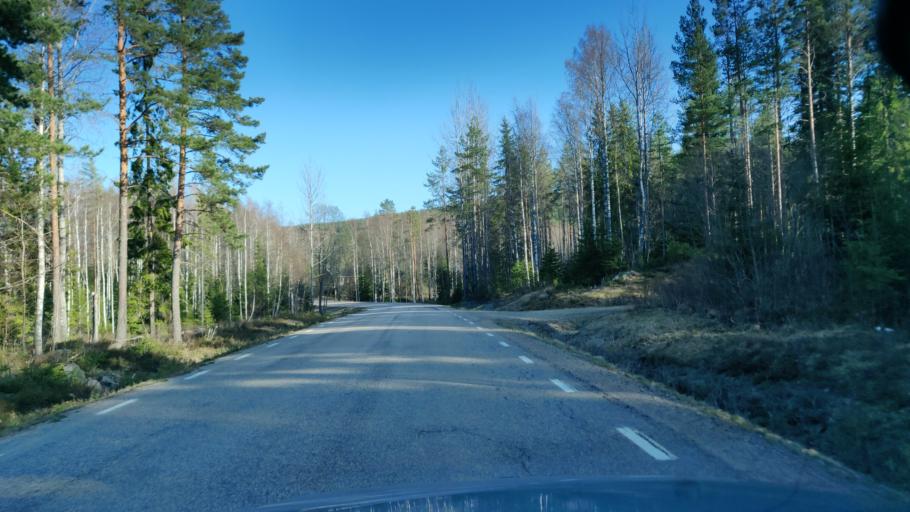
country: SE
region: Vaermland
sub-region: Hagfors Kommun
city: Ekshaerad
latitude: 59.9832
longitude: 13.3564
